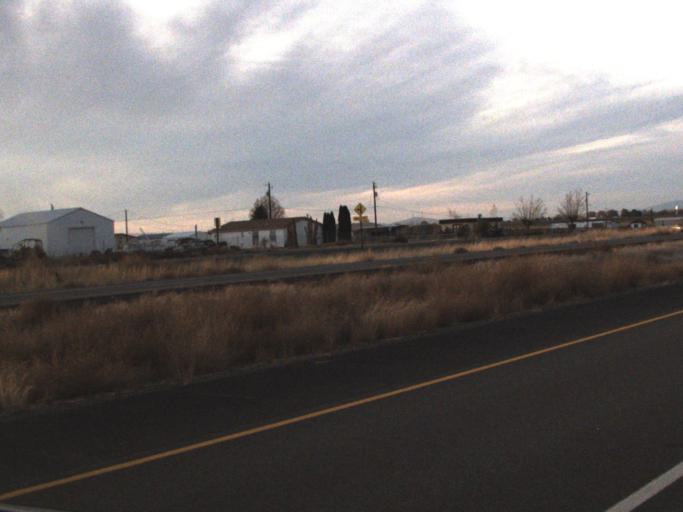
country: US
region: Washington
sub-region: Walla Walla County
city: Burbank
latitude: 46.1828
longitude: -118.9746
